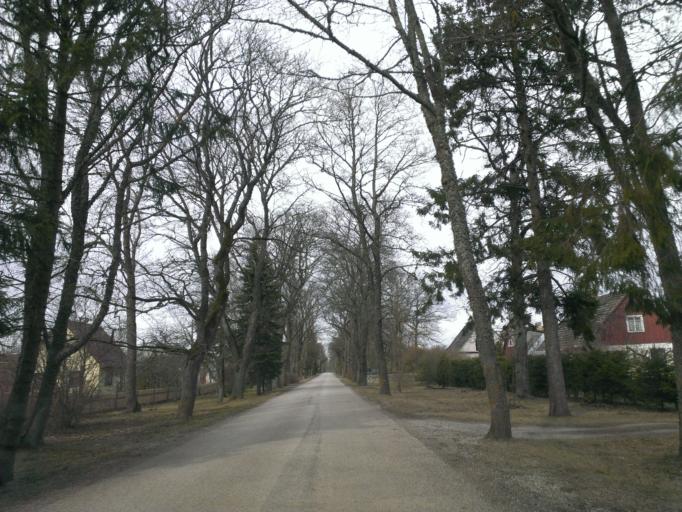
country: EE
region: Laeaene
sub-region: Lihula vald
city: Lihula
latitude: 58.5825
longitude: 23.5371
